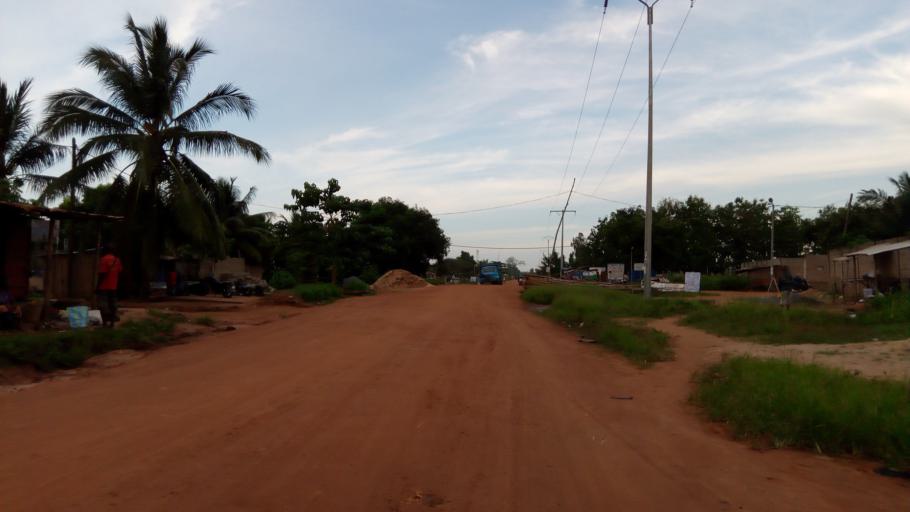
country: TG
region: Maritime
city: Lome
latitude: 6.2561
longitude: 1.1390
